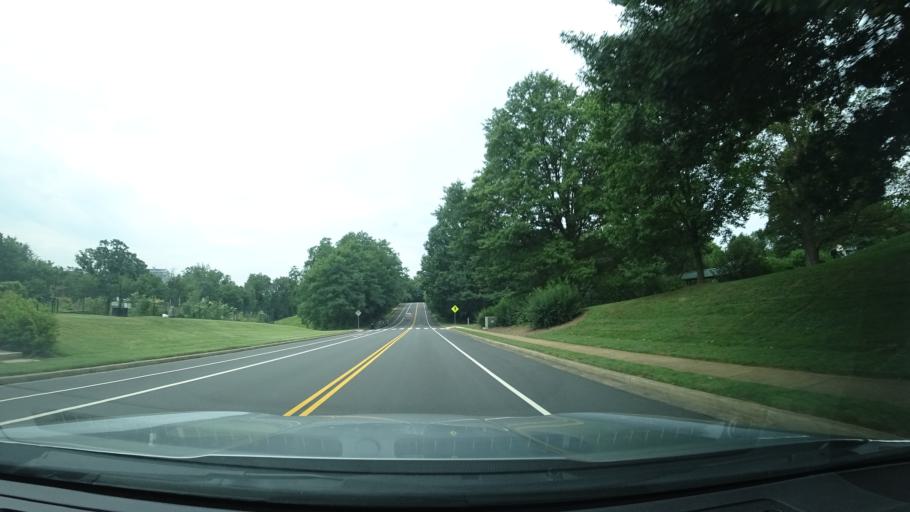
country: US
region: Virginia
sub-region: Fairfax County
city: Reston
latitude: 38.9581
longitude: -77.3388
